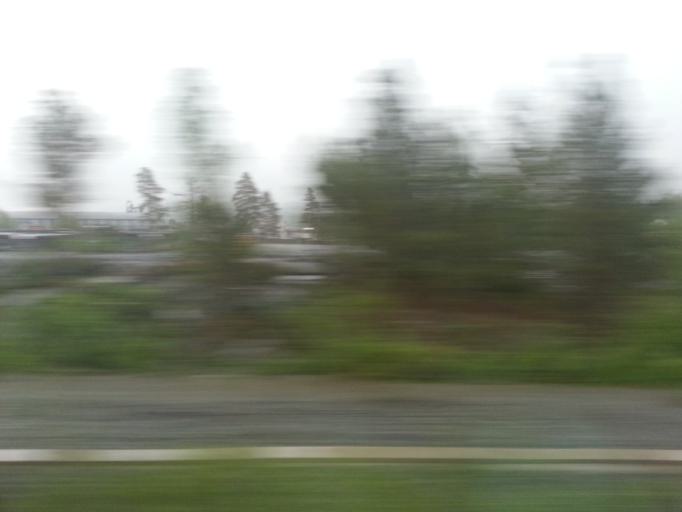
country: NO
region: Sor-Trondelag
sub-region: Oppdal
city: Oppdal
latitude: 62.5877
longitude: 9.6819
